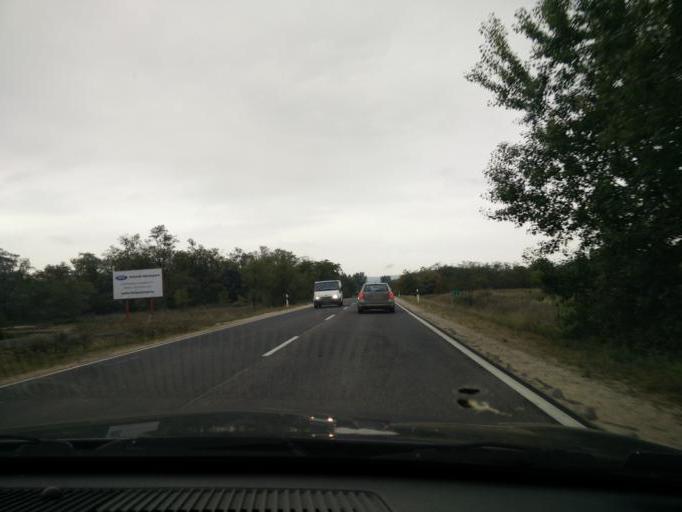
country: HU
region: Komarom-Esztergom
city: Kesztolc
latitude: 47.7143
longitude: 18.7727
